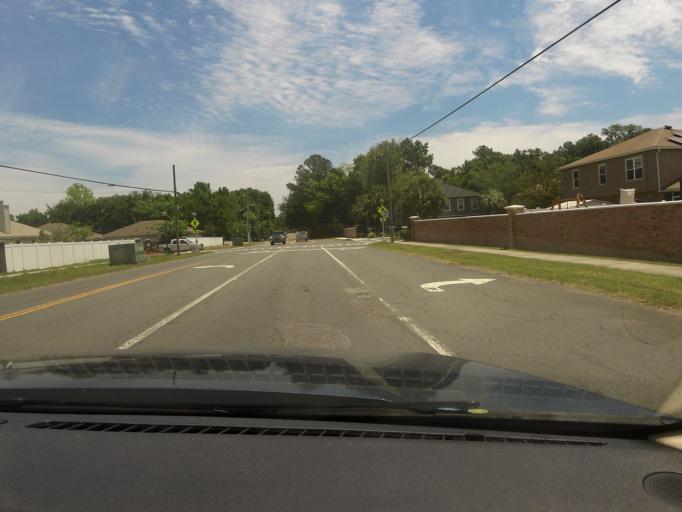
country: US
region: Florida
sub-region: Duval County
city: Jacksonville
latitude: 30.4629
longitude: -81.5700
